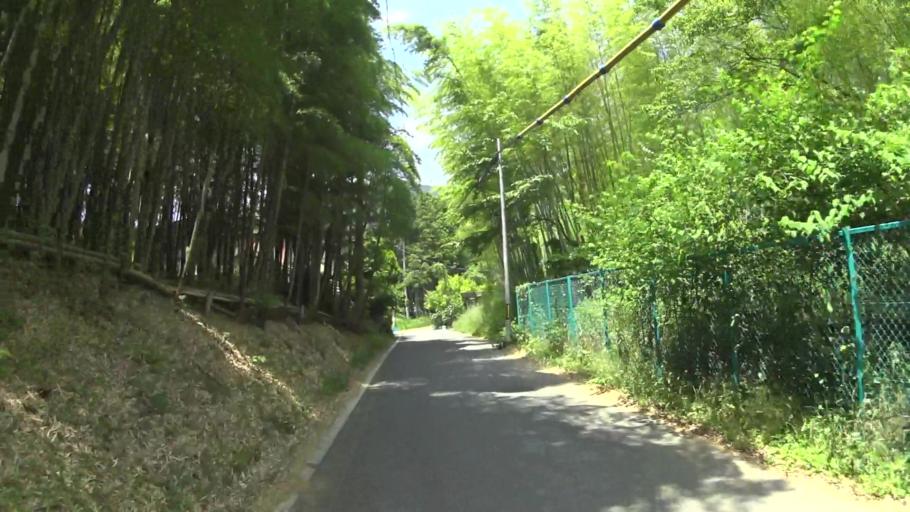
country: JP
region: Kyoto
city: Muko
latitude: 34.9630
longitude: 135.6567
